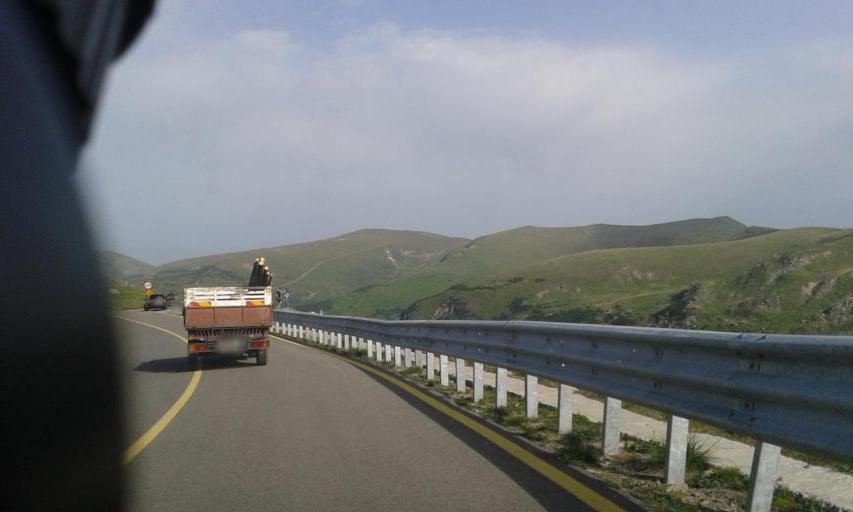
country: RO
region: Gorj
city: Novaci-Straini
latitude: 45.3614
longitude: 23.6573
